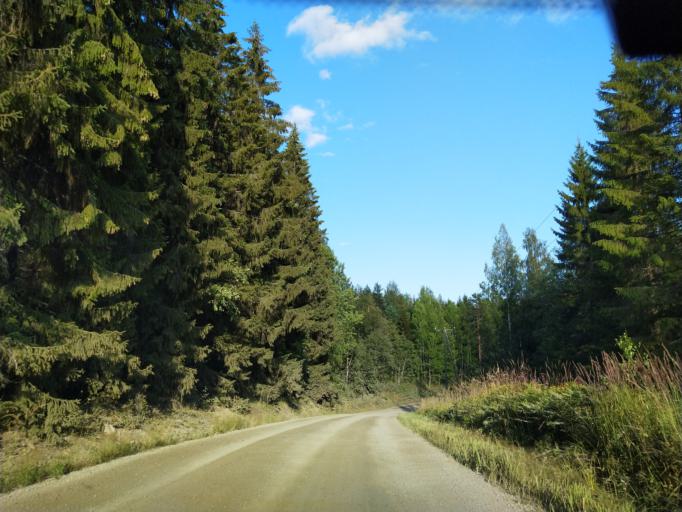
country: FI
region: Central Finland
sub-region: Jaemsae
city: Kuhmoinen
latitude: 61.6940
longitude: 24.9445
